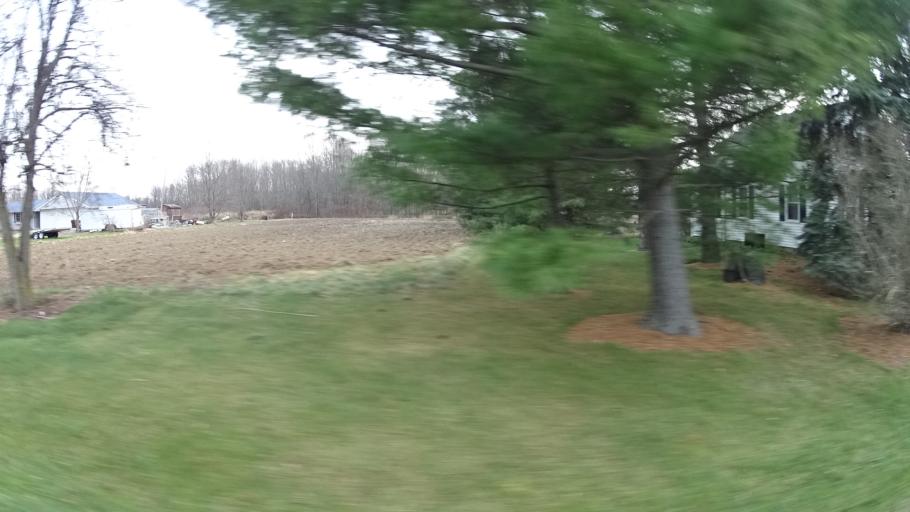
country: US
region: Ohio
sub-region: Lorain County
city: Wellington
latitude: 41.1865
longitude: -82.1689
